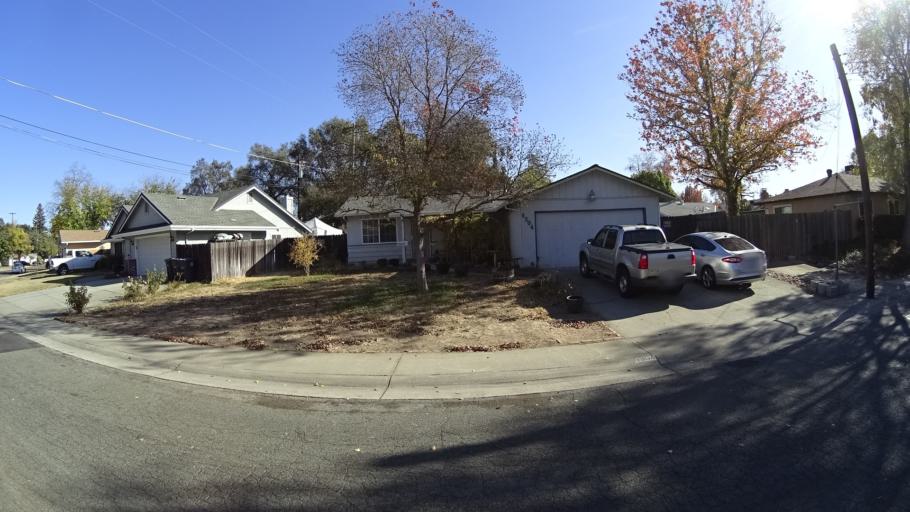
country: US
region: California
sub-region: Sacramento County
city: Antelope
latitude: 38.6863
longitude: -121.3174
